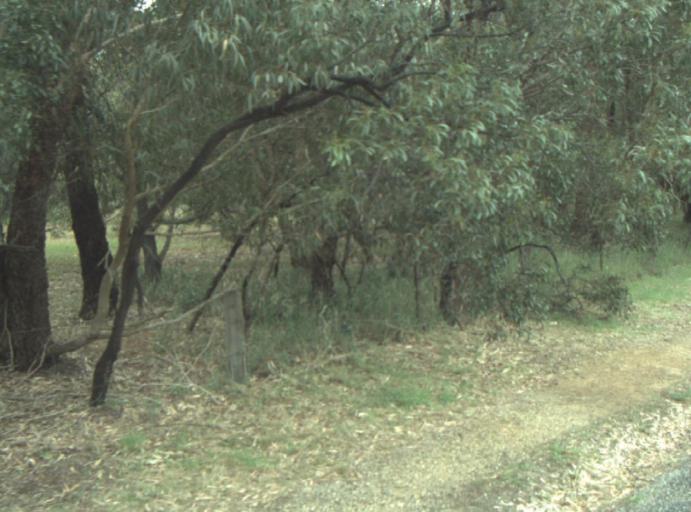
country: AU
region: Victoria
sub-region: Greater Geelong
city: Leopold
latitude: -38.2047
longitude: 144.4190
